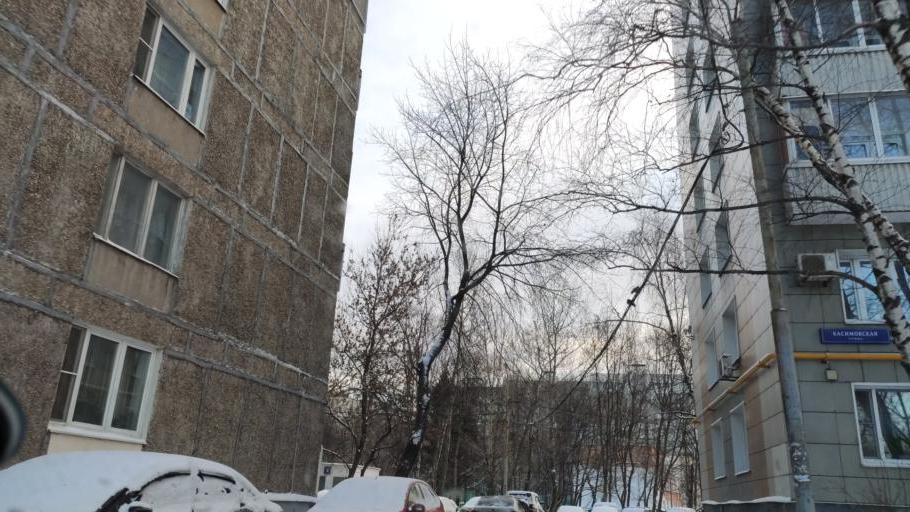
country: RU
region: Moskovskaya
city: Biryulevo Zapadnoye
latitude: 55.6002
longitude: 37.6534
